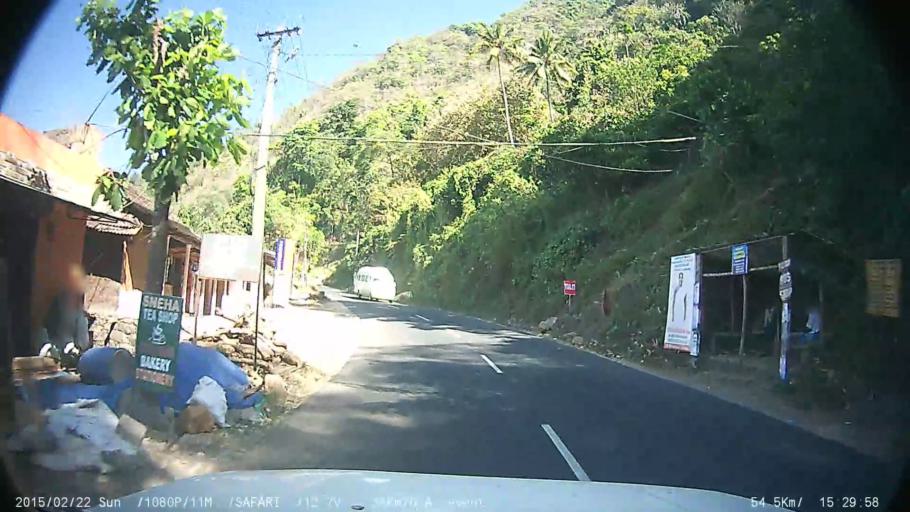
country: IN
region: Kerala
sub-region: Kottayam
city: Erattupetta
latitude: 9.5589
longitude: 76.9509
